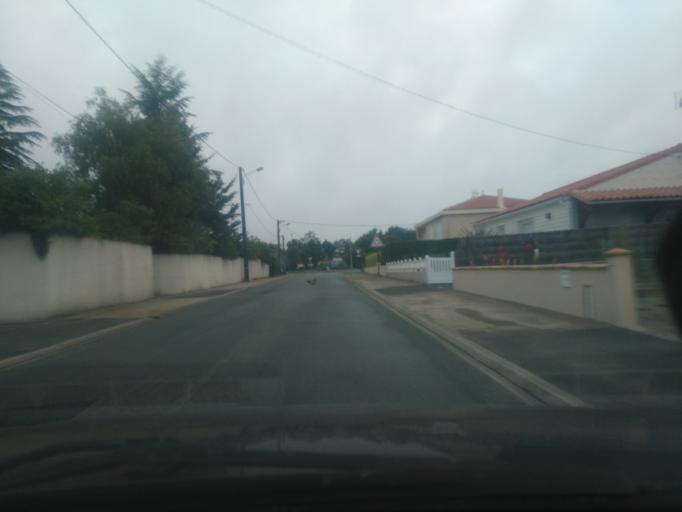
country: FR
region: Pays de la Loire
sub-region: Departement de la Vendee
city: La Ferriere
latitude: 46.7174
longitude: -1.3152
